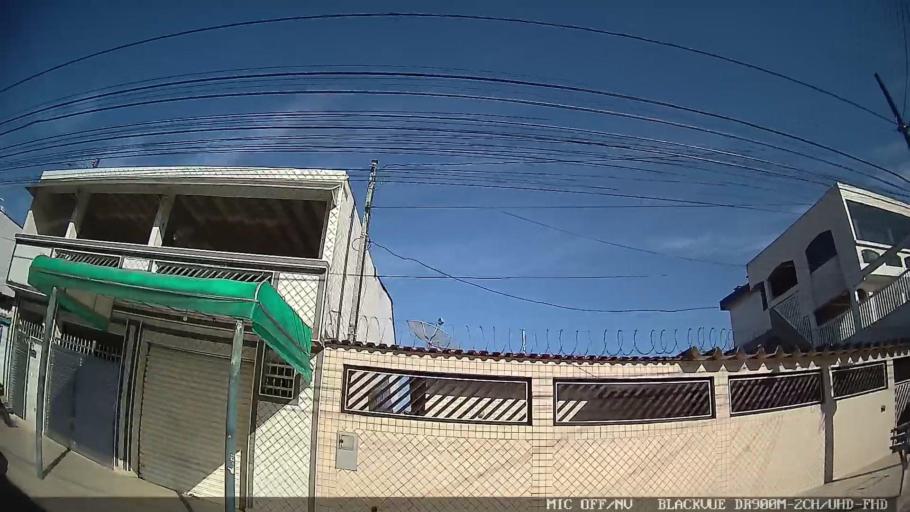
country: BR
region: Sao Paulo
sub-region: Guaruja
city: Guaruja
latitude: -23.9569
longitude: -46.2837
